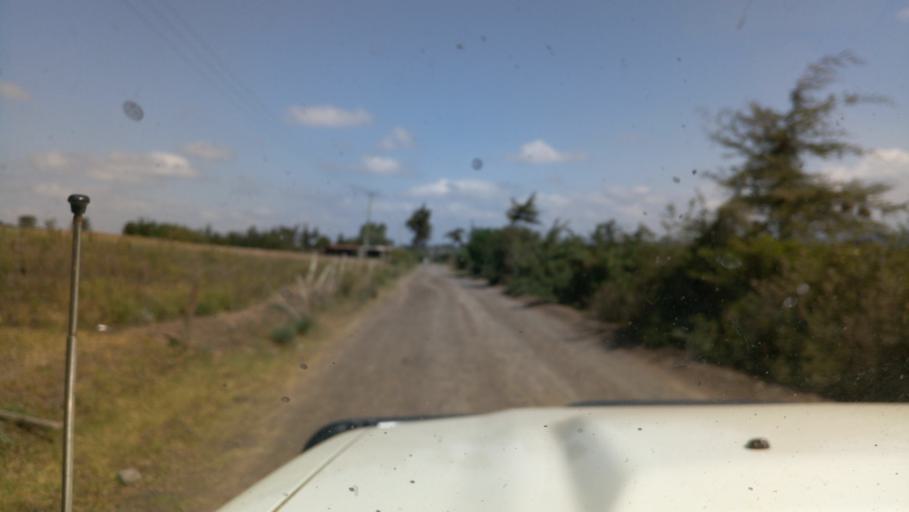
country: KE
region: Nyeri
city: Nyeri
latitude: -0.2625
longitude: 36.8122
